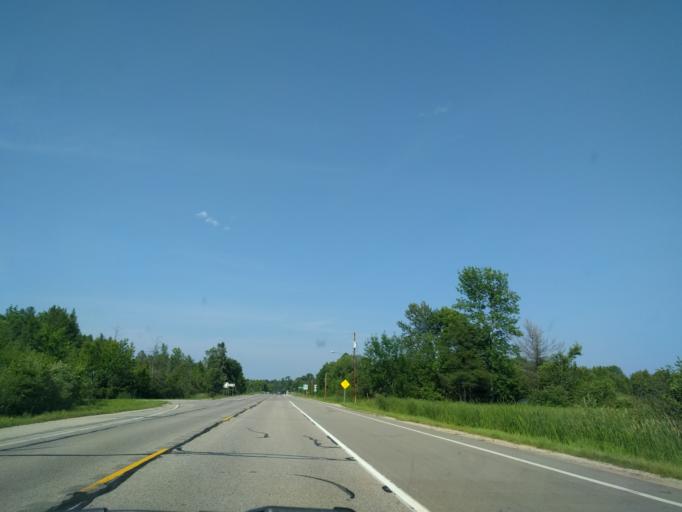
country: US
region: Michigan
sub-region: Delta County
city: Escanaba
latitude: 45.6757
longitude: -87.1461
